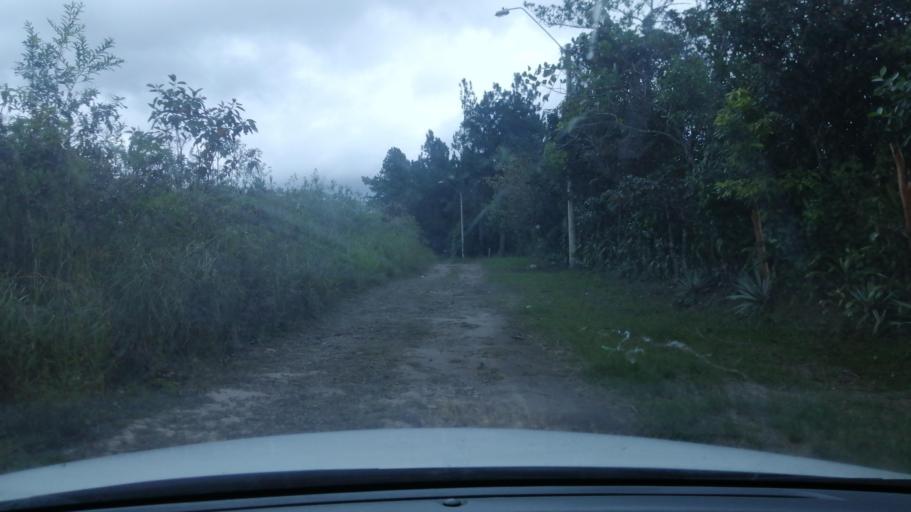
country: PA
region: Chiriqui
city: Potrerillos Arriba
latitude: 8.6851
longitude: -82.4549
